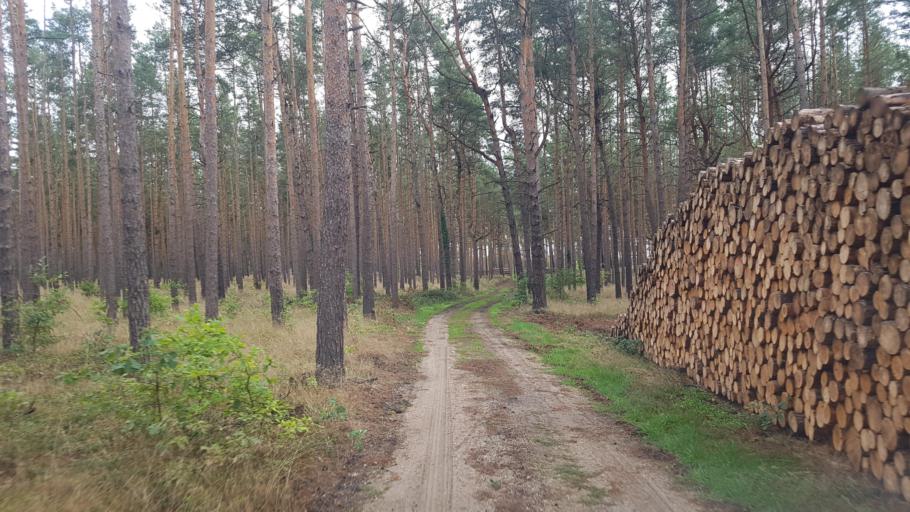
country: DE
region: Brandenburg
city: Elsterwerda
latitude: 51.4855
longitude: 13.4624
